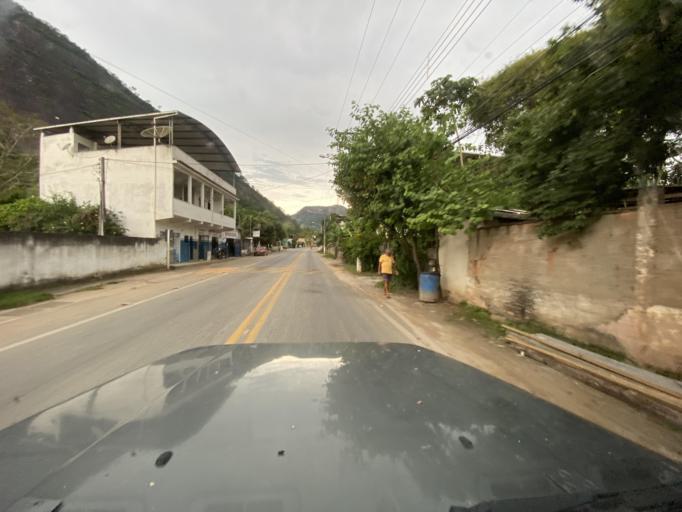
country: BR
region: Espirito Santo
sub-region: Jeronimo Monteiro
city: Jeronimo Monteiro
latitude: -20.7952
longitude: -41.3760
